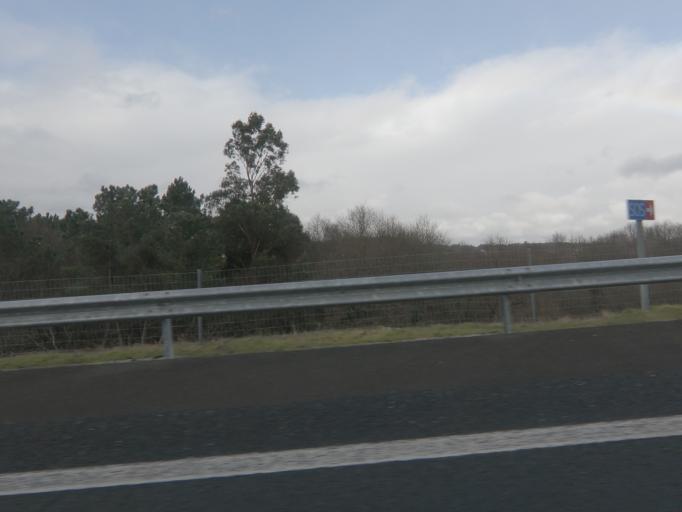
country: ES
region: Galicia
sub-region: Provincia da Coruna
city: Ribeira
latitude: 42.7460
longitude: -8.3790
